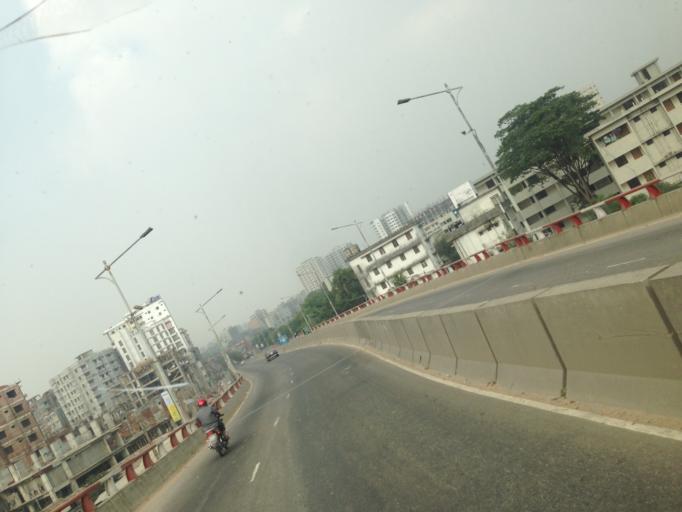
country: BD
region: Dhaka
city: Tungi
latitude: 23.8171
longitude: 90.3982
